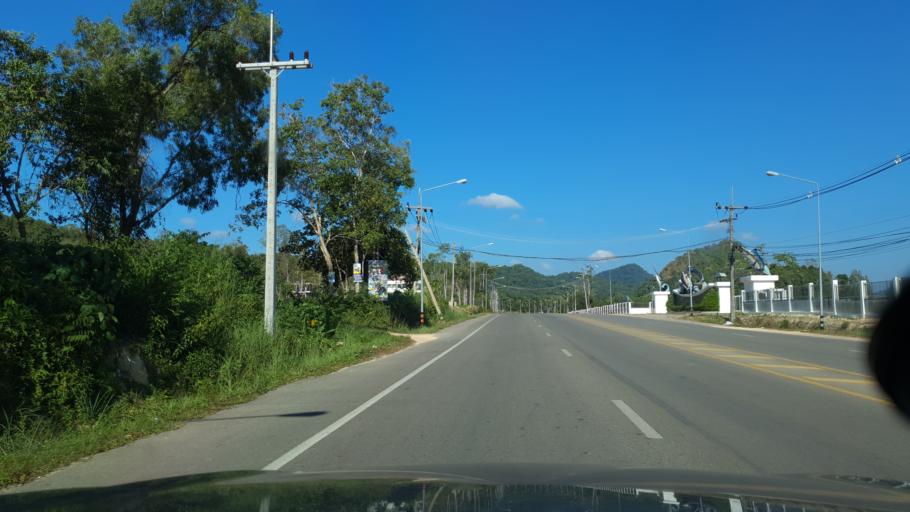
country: TH
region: Phangnga
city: Ban Ao Nang
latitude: 8.0396
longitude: 98.8510
